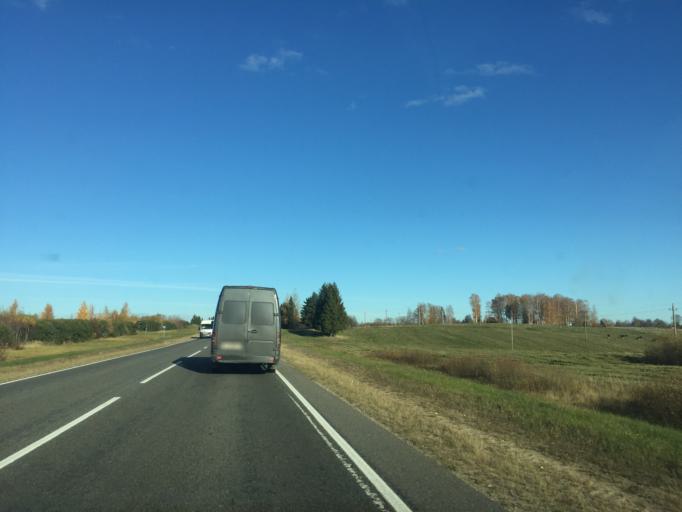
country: BY
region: Vitebsk
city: Dzisna
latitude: 55.2946
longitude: 28.2019
